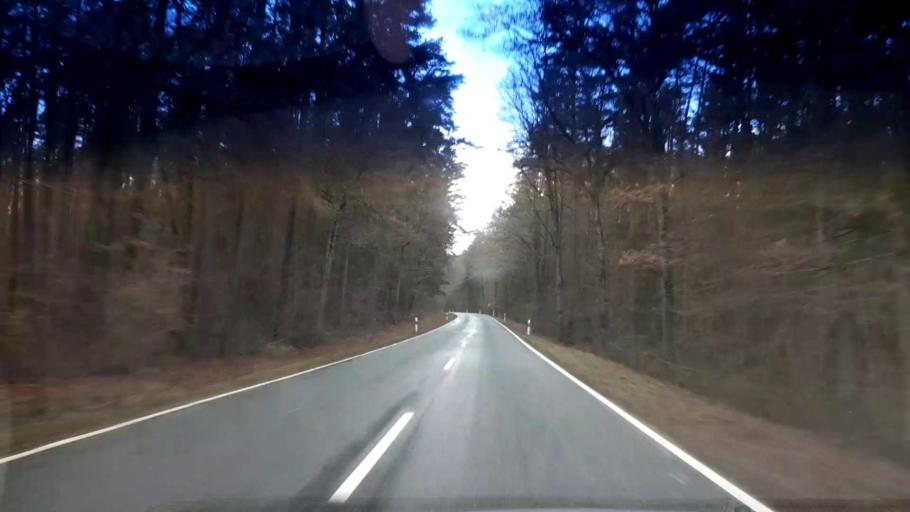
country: DE
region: Bavaria
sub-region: Upper Franconia
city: Lauter
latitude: 49.9649
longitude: 10.7618
